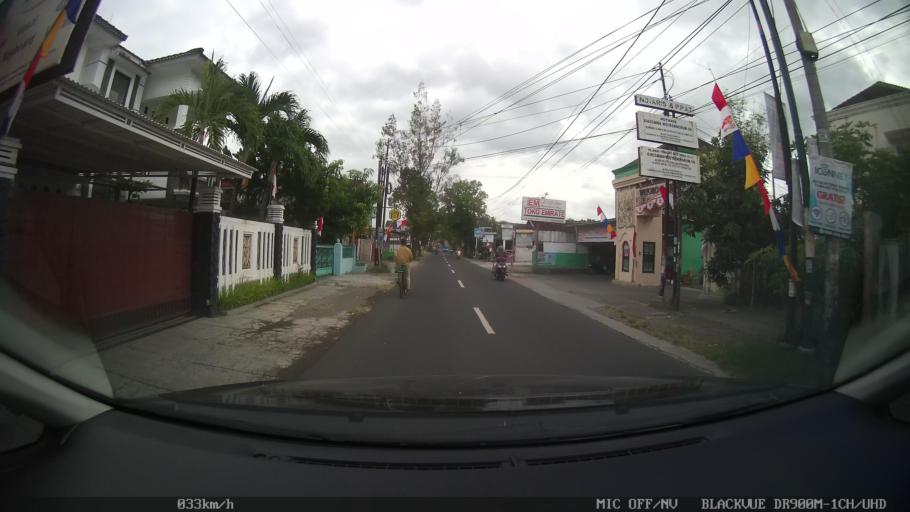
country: ID
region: Daerah Istimewa Yogyakarta
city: Depok
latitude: -7.8265
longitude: 110.4137
